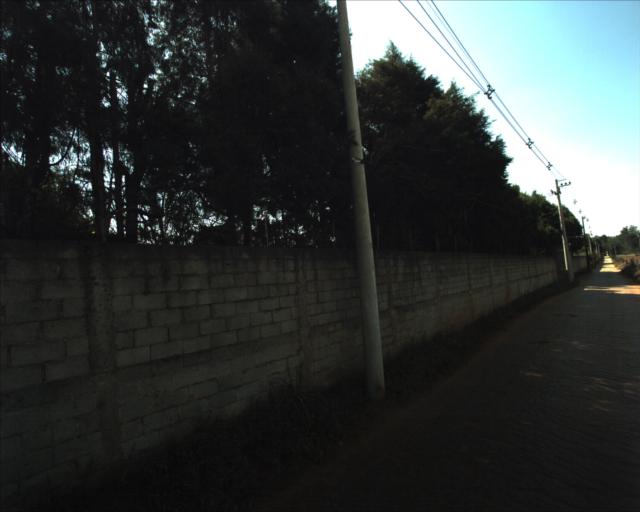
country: BR
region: Sao Paulo
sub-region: Aracoiaba Da Serra
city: Aracoiaba da Serra
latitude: -23.4846
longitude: -47.5408
